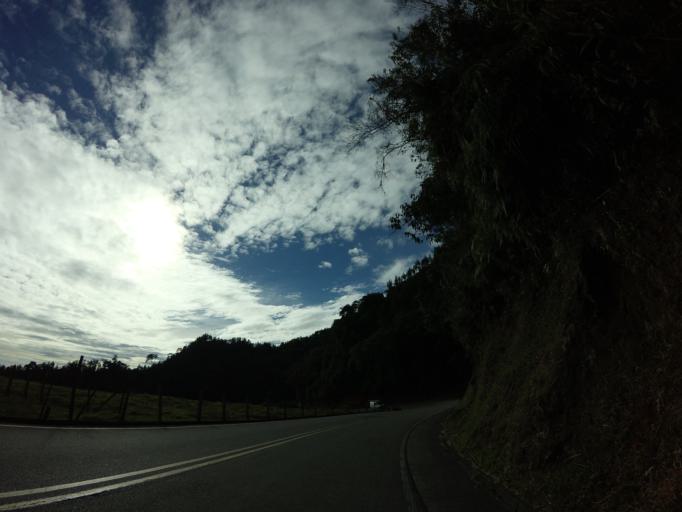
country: CO
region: Tolima
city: Herveo
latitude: 5.1429
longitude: -75.1563
